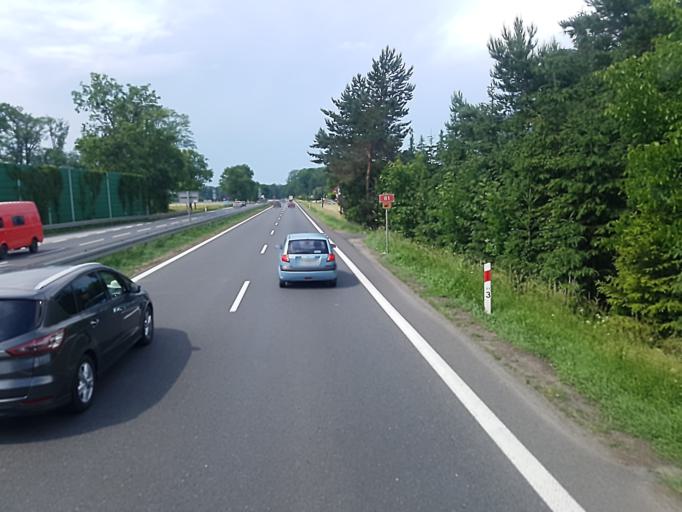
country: PL
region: Silesian Voivodeship
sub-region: Powiat cieszynski
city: Ochaby
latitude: 49.8528
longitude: 18.7606
